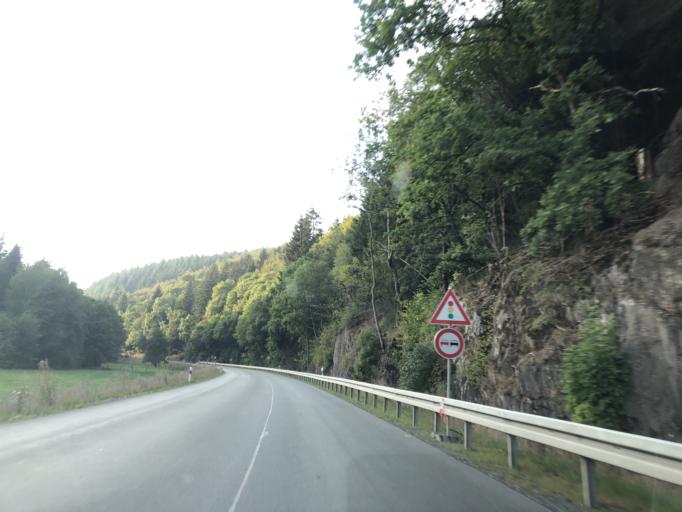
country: DE
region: North Rhine-Westphalia
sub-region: Regierungsbezirk Arnsberg
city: Winterberg
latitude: 51.1677
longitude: 8.5552
